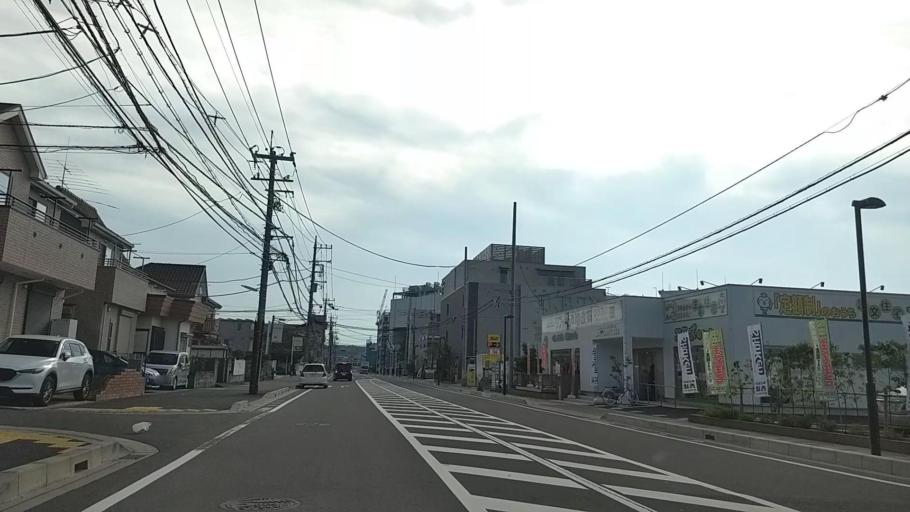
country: JP
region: Kanagawa
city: Zama
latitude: 35.4584
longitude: 139.3873
